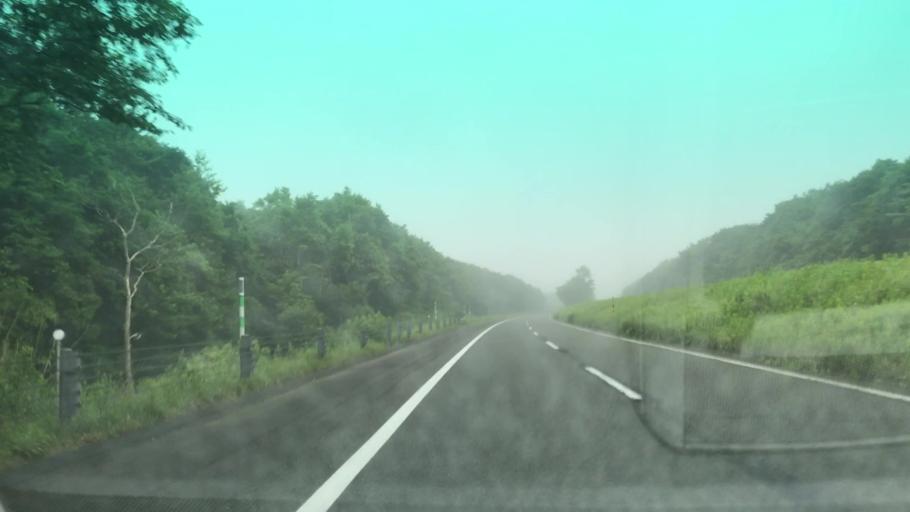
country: JP
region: Hokkaido
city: Chitose
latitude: 42.7948
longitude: 141.6270
